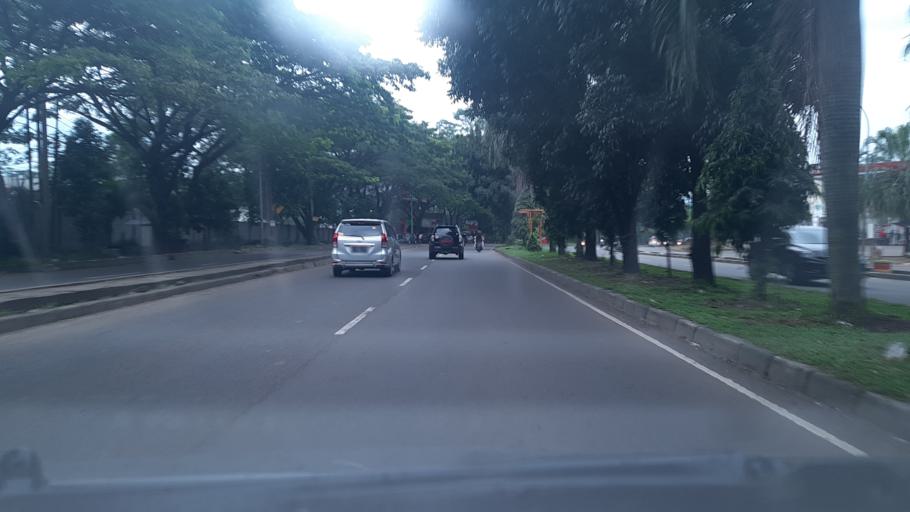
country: ID
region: West Java
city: Cibinong
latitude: -6.5277
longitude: 106.8493
